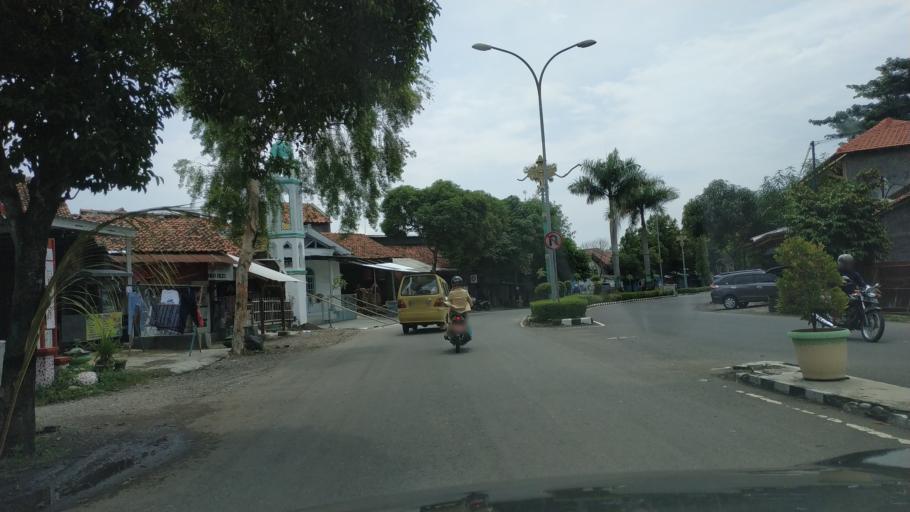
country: ID
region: Central Java
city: Slawi
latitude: -6.9870
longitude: 109.1271
